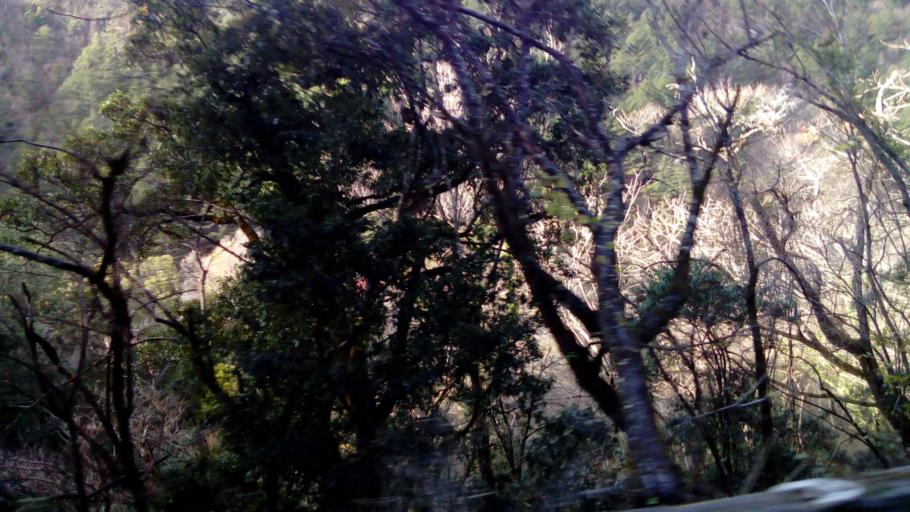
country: TW
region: Taiwan
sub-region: Hualien
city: Hualian
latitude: 24.3475
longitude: 121.3167
